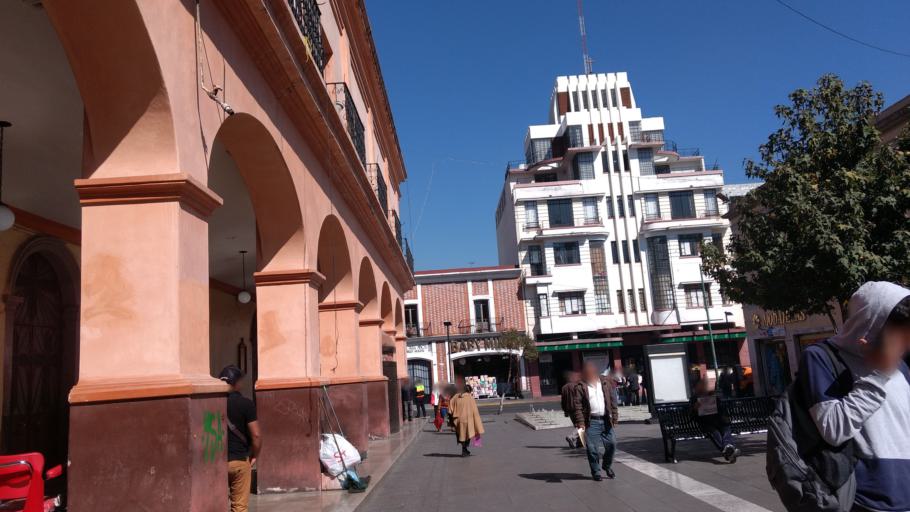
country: MX
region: Mexico
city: Toluca
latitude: 19.2917
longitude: -99.6555
